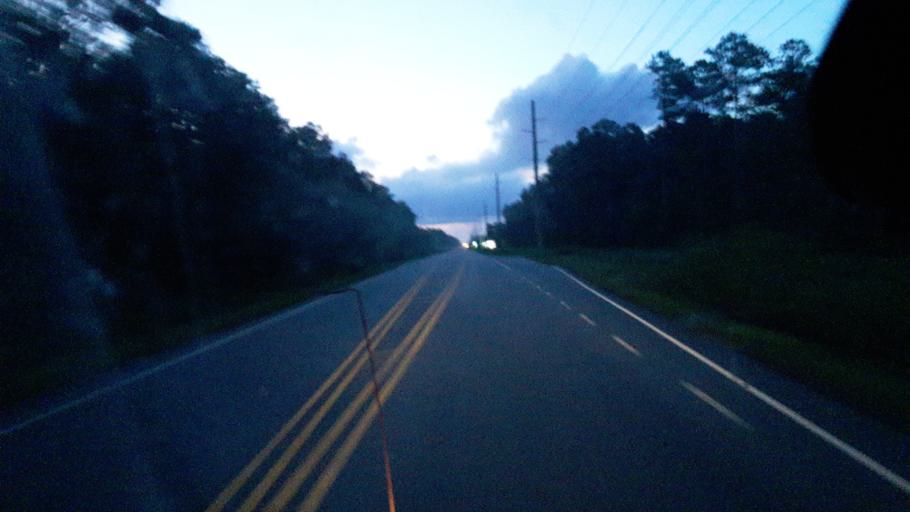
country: US
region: North Carolina
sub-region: Brunswick County
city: Oak Island
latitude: 33.9892
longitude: -78.2026
